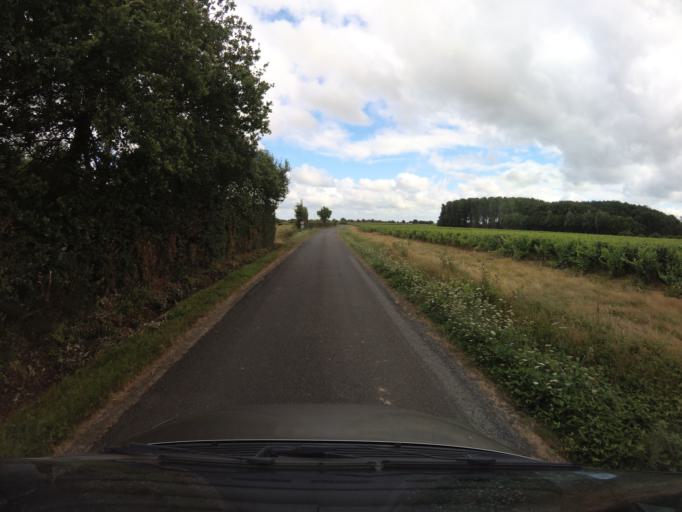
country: FR
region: Pays de la Loire
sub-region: Departement de la Vendee
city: Saint-Philbert-de-Bouaine
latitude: 47.0044
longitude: -1.5297
